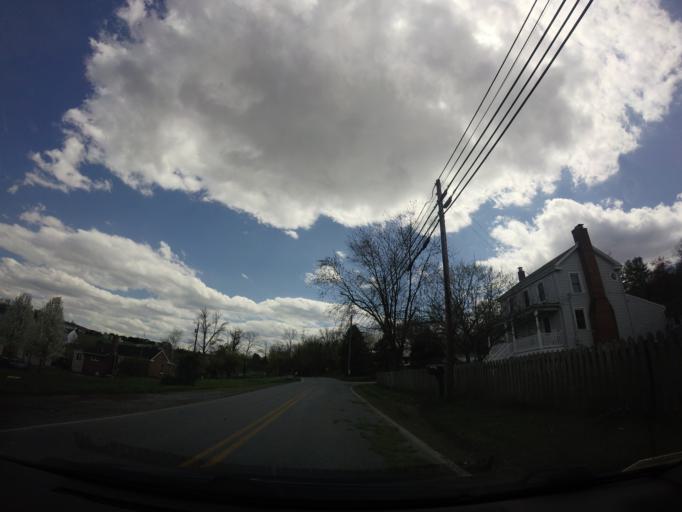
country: US
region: Maryland
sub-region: Washington County
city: Keedysville
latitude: 39.4315
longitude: -77.6780
